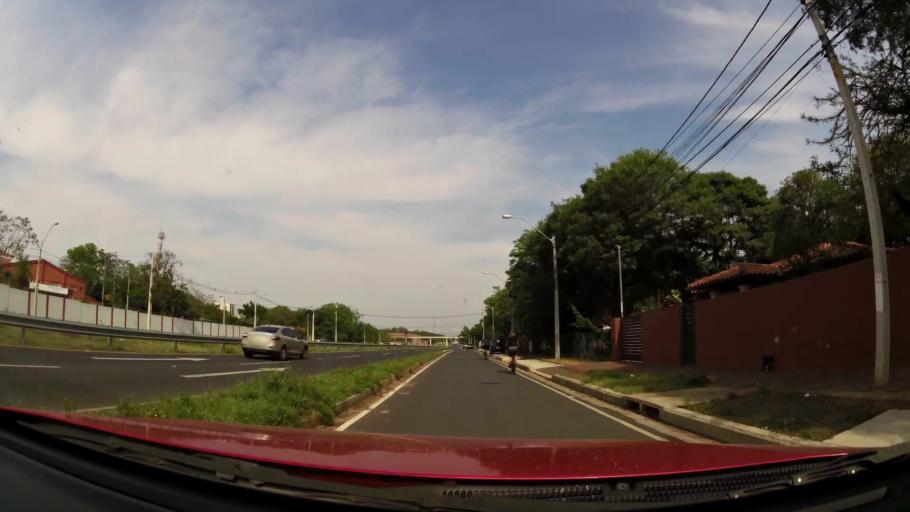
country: PY
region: Central
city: Fernando de la Mora
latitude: -25.2564
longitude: -57.5561
